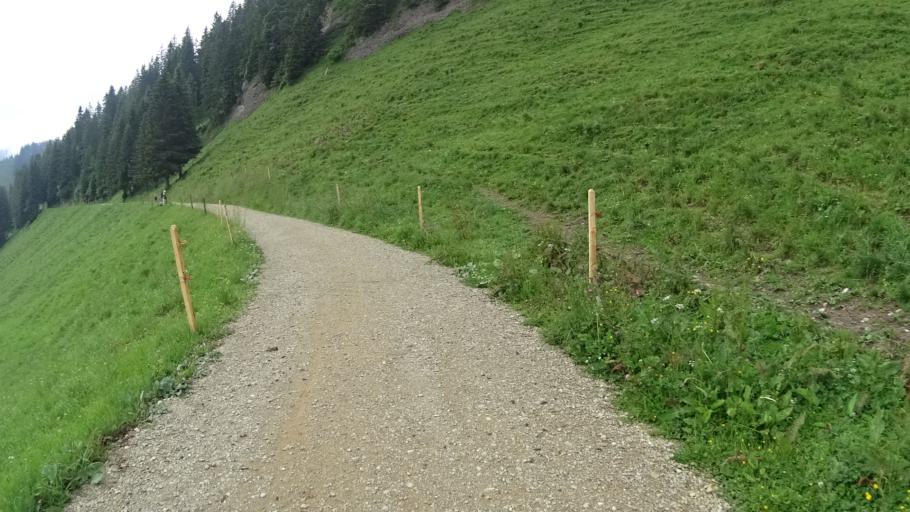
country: CH
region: Lucerne
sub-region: Lucerne-Land District
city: Vitznau
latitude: 47.0465
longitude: 8.4766
